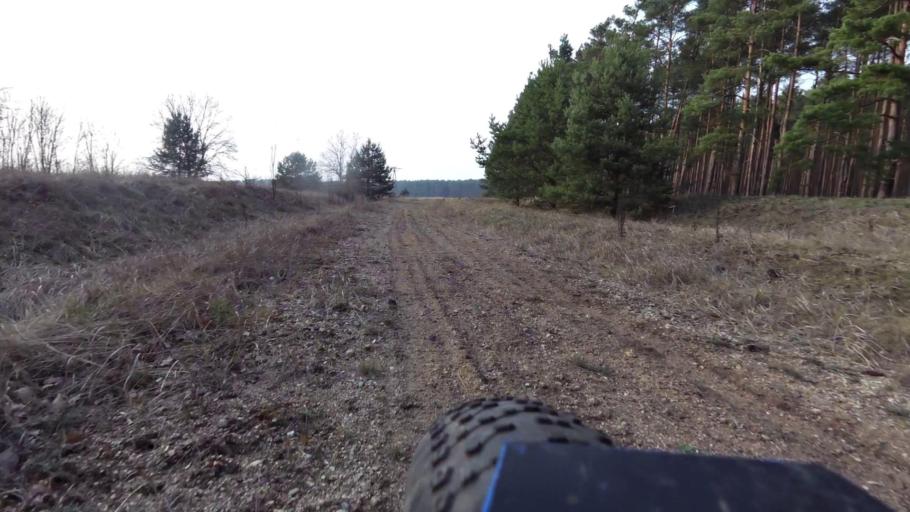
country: DE
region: Brandenburg
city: Vogelsang
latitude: 52.2587
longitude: 14.6934
